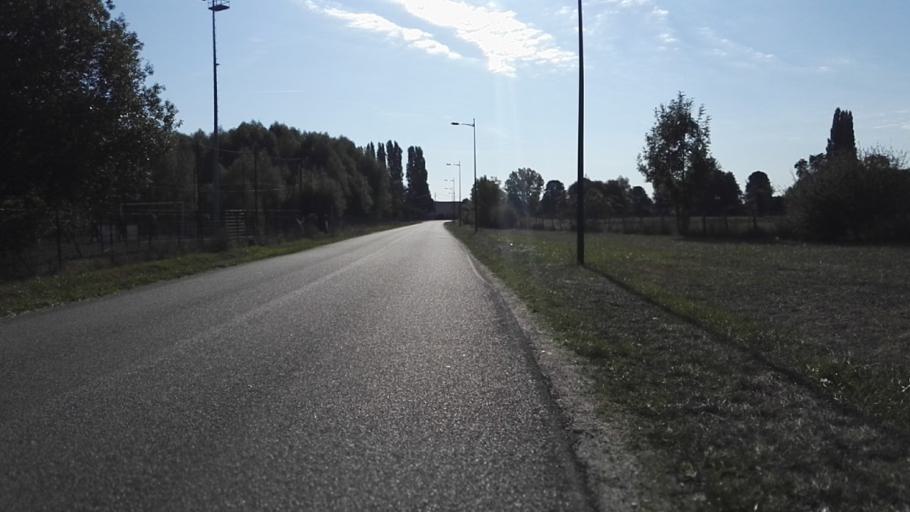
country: FR
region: Haute-Normandie
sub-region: Departement de l'Eure
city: Menilles
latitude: 49.0268
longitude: 1.3694
